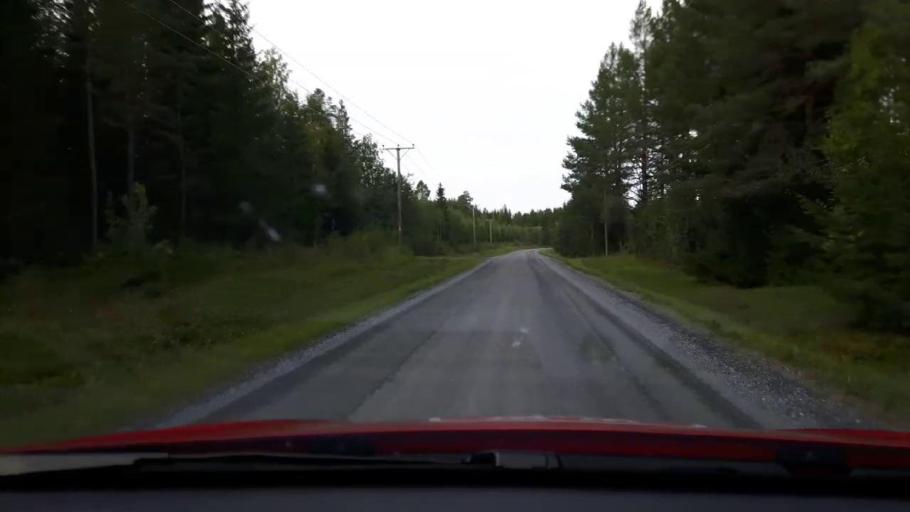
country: SE
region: Jaemtland
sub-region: Krokoms Kommun
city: Valla
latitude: 63.2448
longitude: 13.9700
